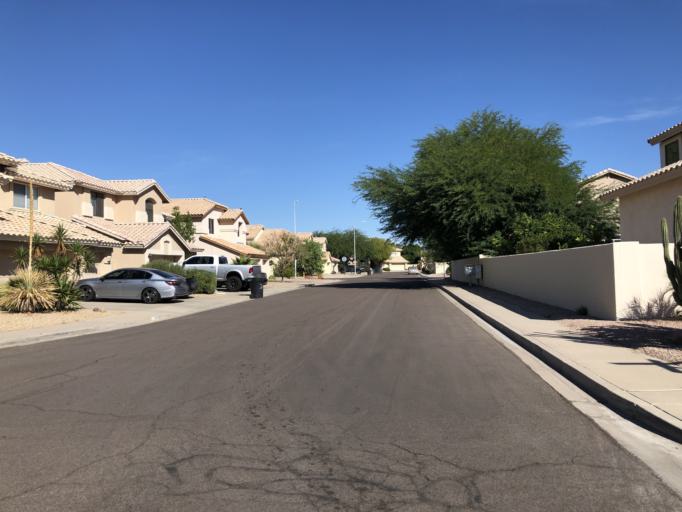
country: US
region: Arizona
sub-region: Maricopa County
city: Guadalupe
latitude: 33.3074
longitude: -111.9233
